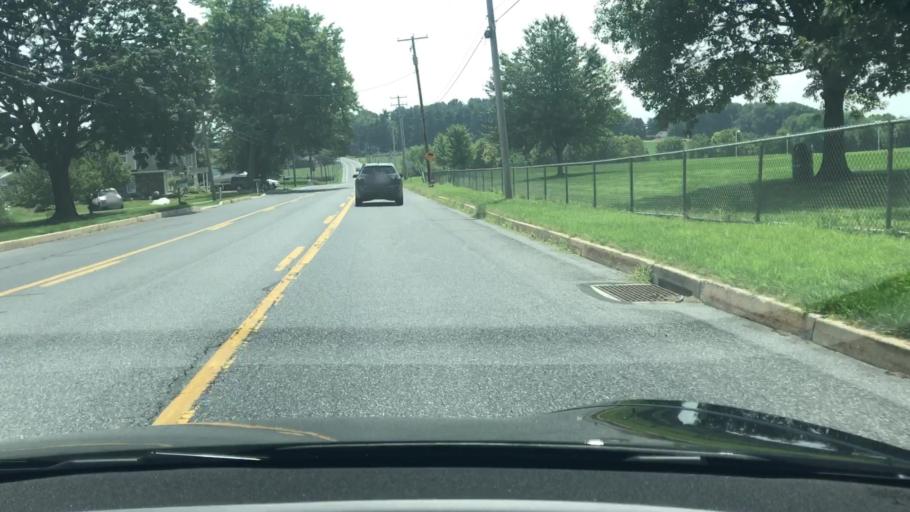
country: US
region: Pennsylvania
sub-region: Lancaster County
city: Landisville
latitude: 40.0861
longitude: -76.4092
